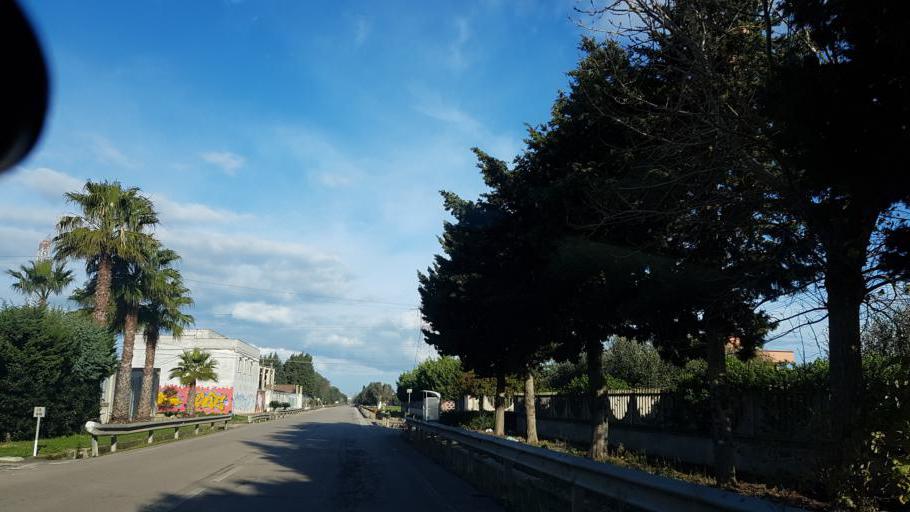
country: IT
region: Apulia
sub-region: Provincia di Brindisi
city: La Rosa
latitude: 40.6017
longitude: 17.9567
